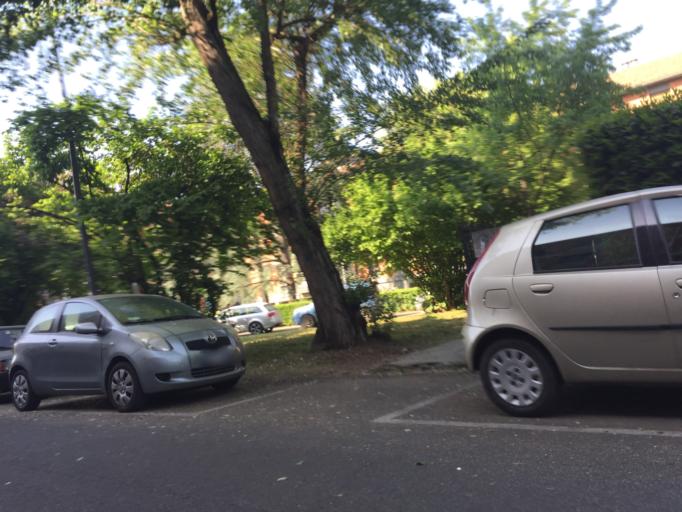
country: IT
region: Lombardy
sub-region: Citta metropolitana di Milano
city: Linate
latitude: 45.4574
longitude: 9.2464
